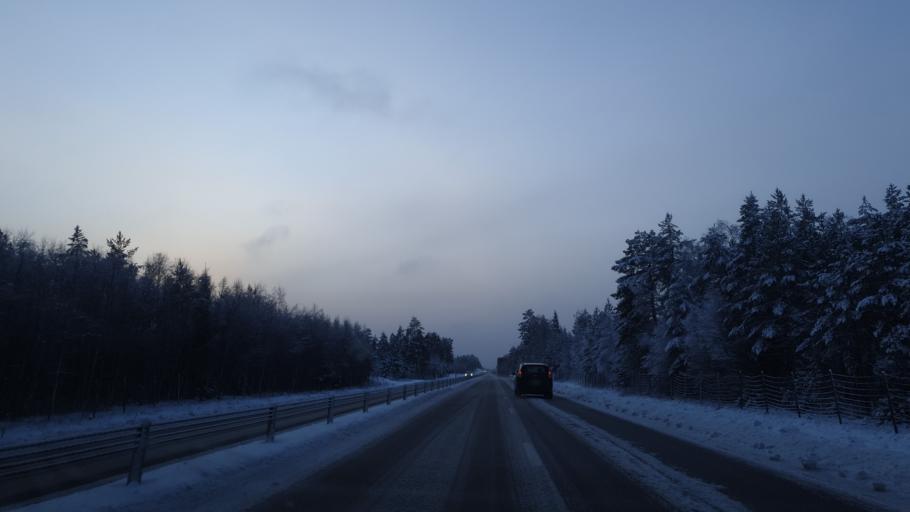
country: SE
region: Vaesterbotten
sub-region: Umea Kommun
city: Saevar
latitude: 63.9468
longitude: 20.6588
